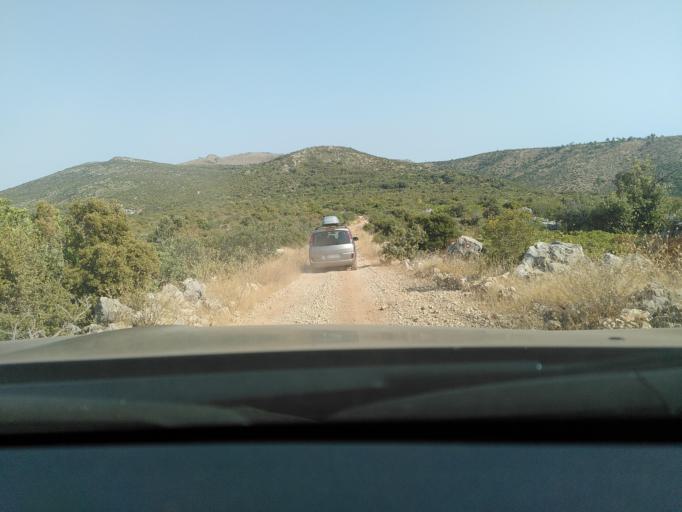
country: HR
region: Splitsko-Dalmatinska
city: Stari Grad
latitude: 43.1635
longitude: 16.5508
